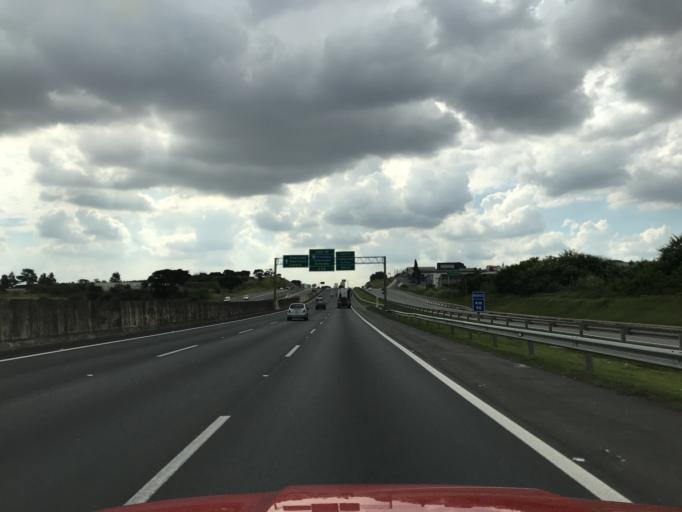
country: BR
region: Sao Paulo
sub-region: Campinas
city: Campinas
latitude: -22.9508
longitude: -47.0620
